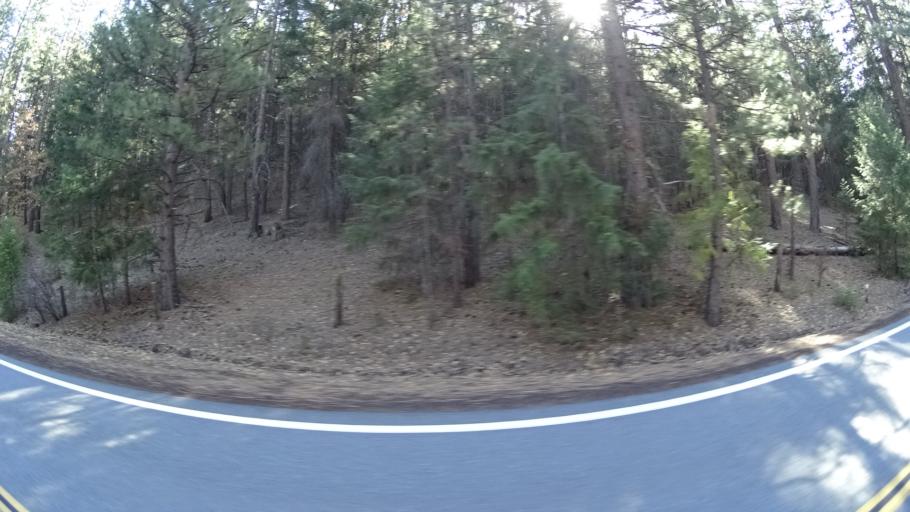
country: US
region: California
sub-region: Siskiyou County
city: Weed
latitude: 41.4640
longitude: -122.6097
